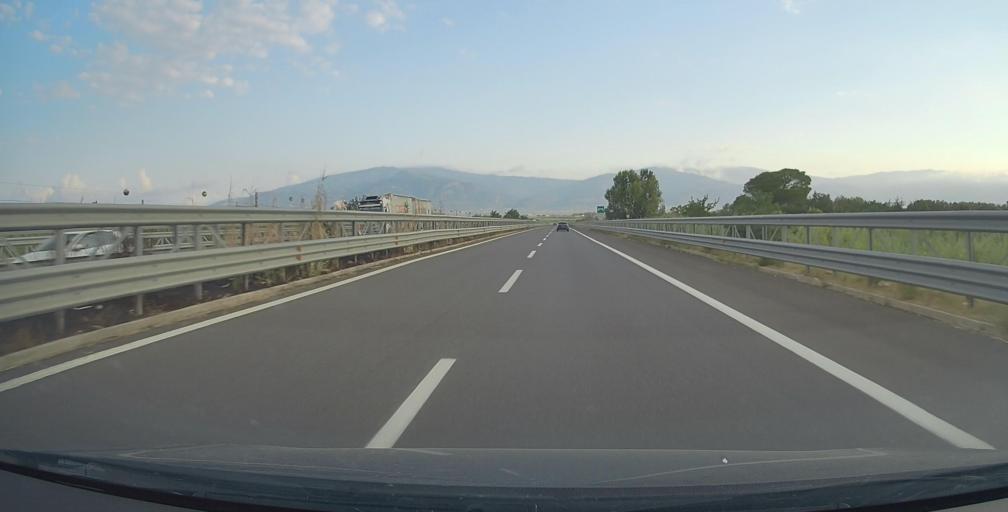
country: IT
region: Calabria
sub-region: Provincia di Catanzaro
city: Santa Eufemia Lamezia
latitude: 38.8929
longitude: 16.2797
